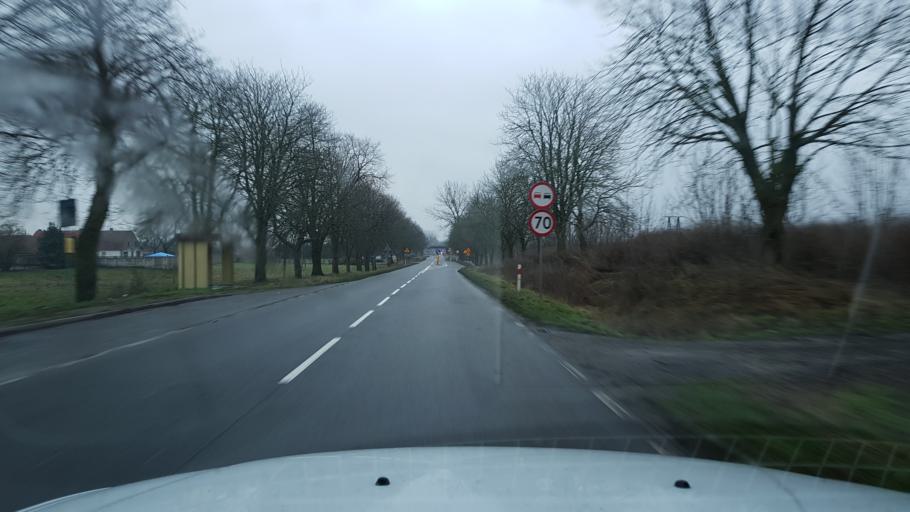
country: PL
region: West Pomeranian Voivodeship
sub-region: Powiat gryficki
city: Ploty
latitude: 53.8231
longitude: 15.2506
